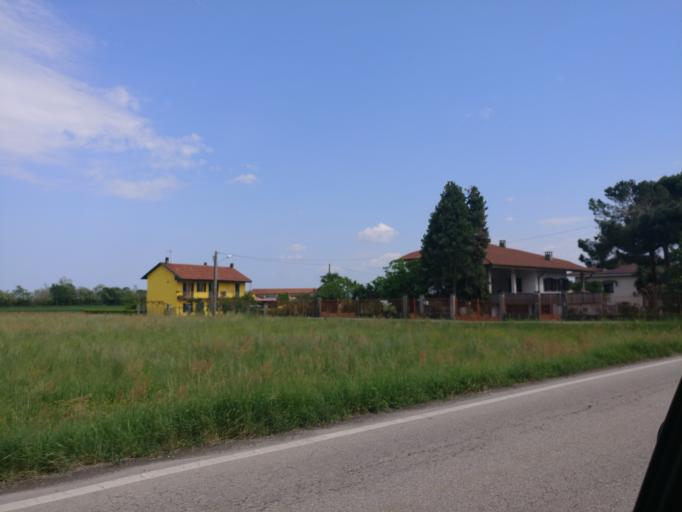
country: IT
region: Piedmont
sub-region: Provincia di Torino
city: Cavour
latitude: 44.7805
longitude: 7.3839
